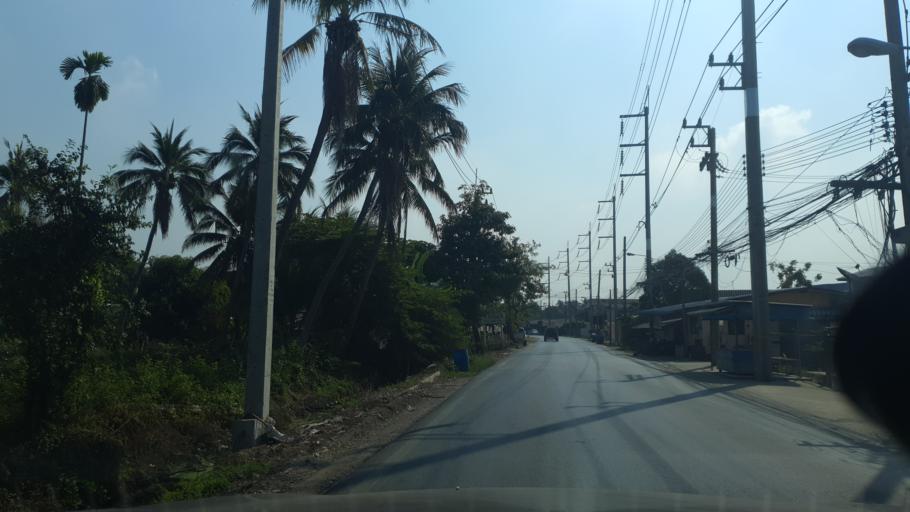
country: TH
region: Nakhon Pathom
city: Salaya
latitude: 13.7754
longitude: 100.2776
